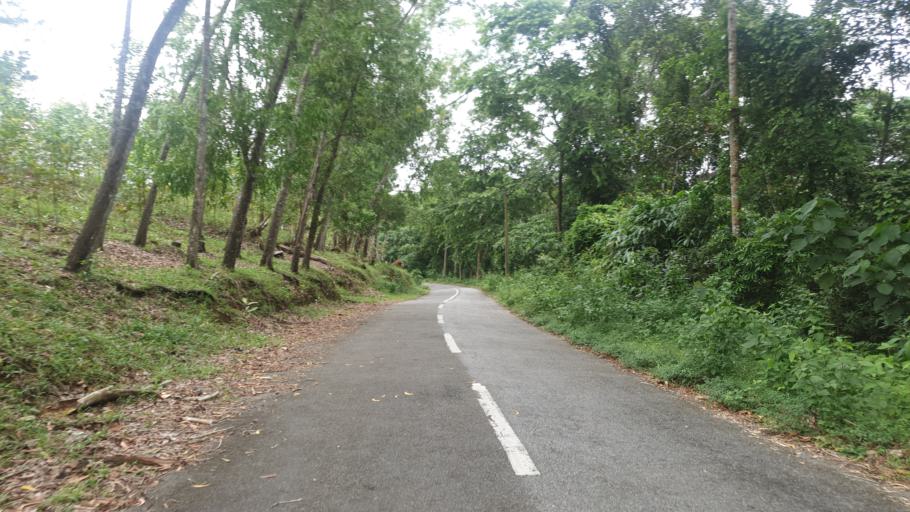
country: IN
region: Kerala
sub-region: Thiruvananthapuram
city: Nedumangad
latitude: 8.6441
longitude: 77.1097
